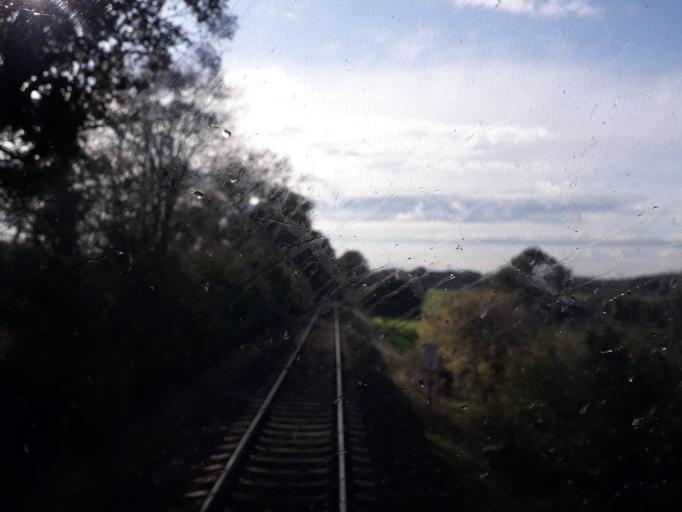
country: DE
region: Brandenburg
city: Gross Pankow
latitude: 53.1319
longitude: 12.0954
